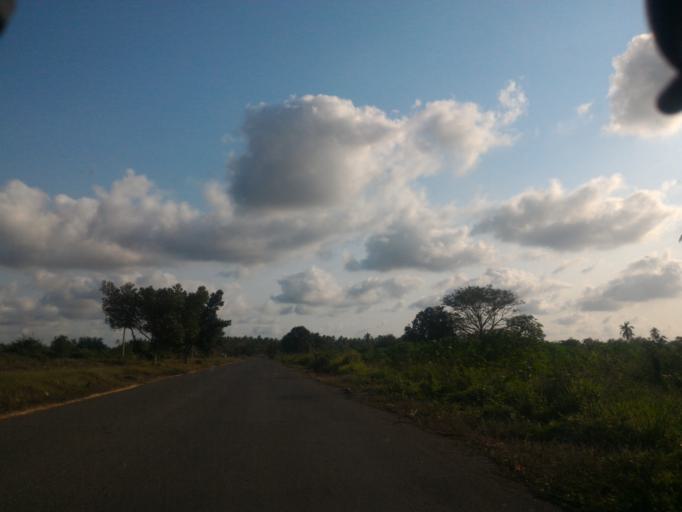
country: MX
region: Colima
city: Tecoman
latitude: 18.9127
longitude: -103.8541
